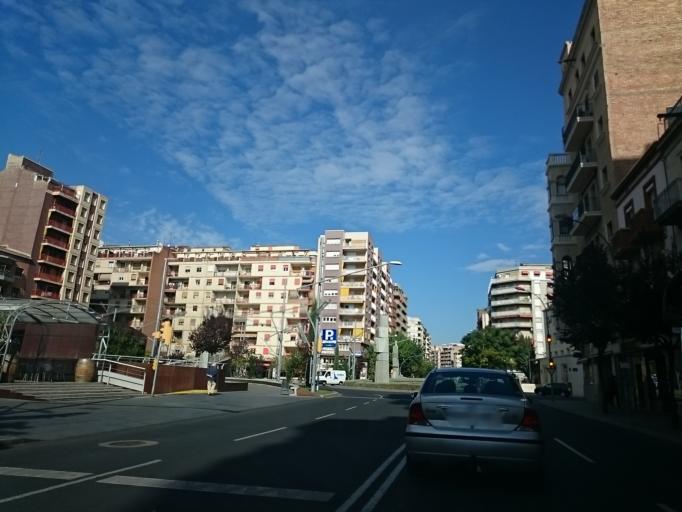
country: ES
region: Catalonia
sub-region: Provincia de Lleida
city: Lleida
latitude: 41.6186
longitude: 0.6196
